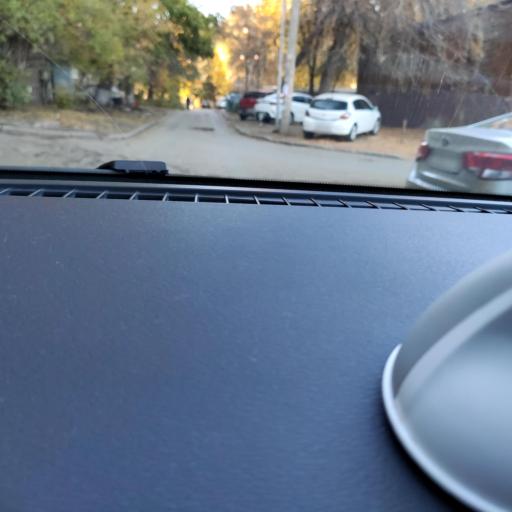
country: RU
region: Samara
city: Samara
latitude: 53.2391
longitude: 50.2214
